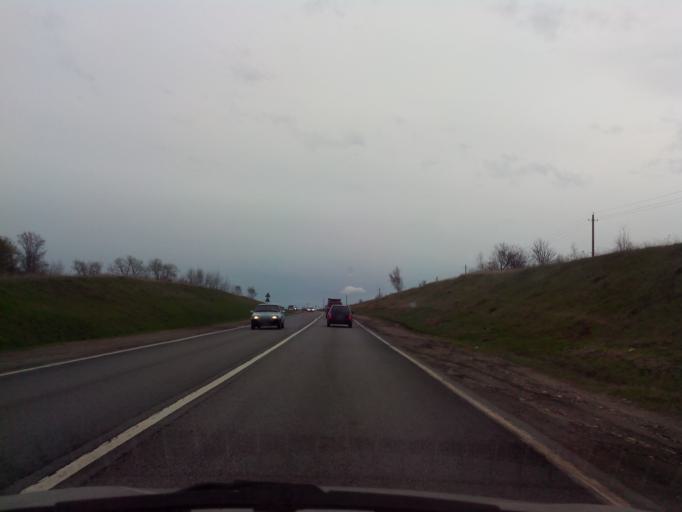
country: RU
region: Moskovskaya
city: Ozherel'ye
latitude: 54.6819
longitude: 38.3224
